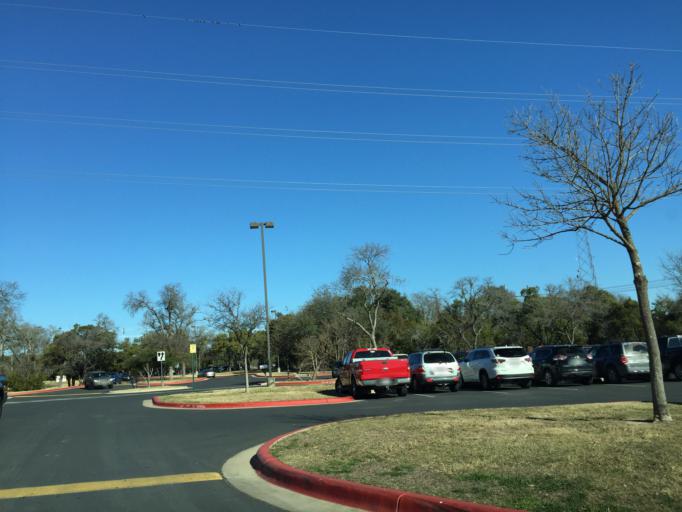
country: US
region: Texas
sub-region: Williamson County
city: Cedar Park
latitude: 30.4938
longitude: -97.8090
